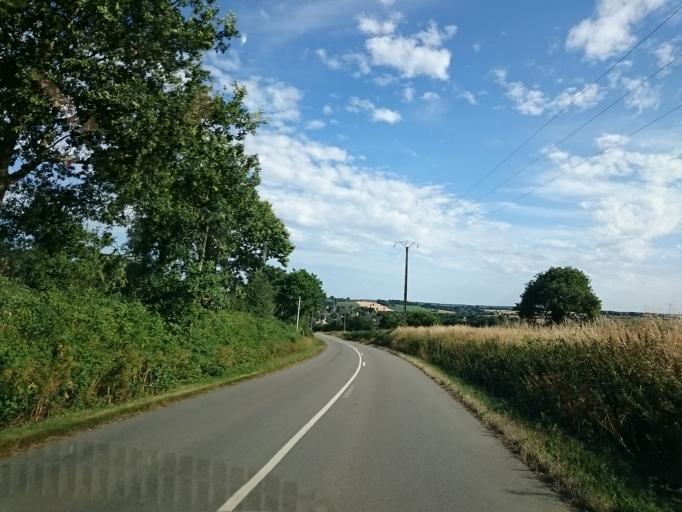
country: FR
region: Brittany
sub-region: Departement d'Ille-et-Vilaine
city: Pance
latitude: 47.9032
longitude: -1.6166
